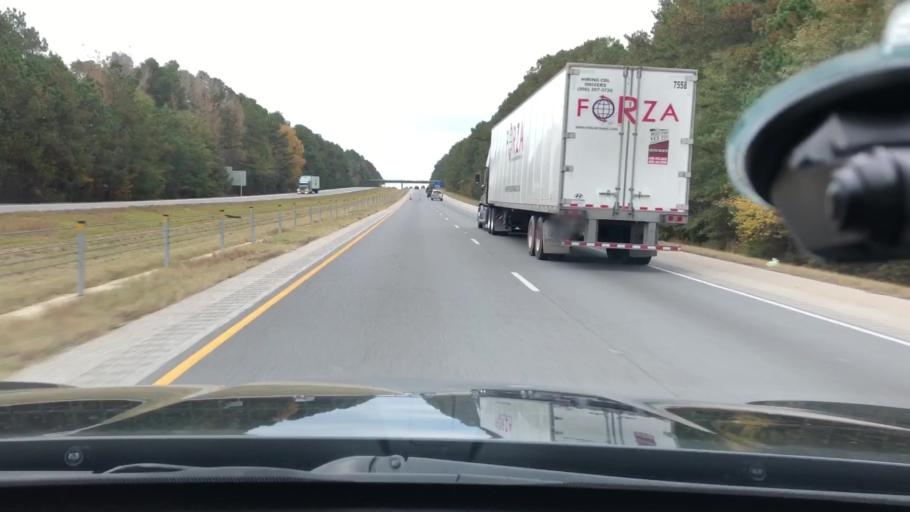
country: US
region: Arkansas
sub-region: Clark County
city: Arkadelphia
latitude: 34.0876
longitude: -93.1111
